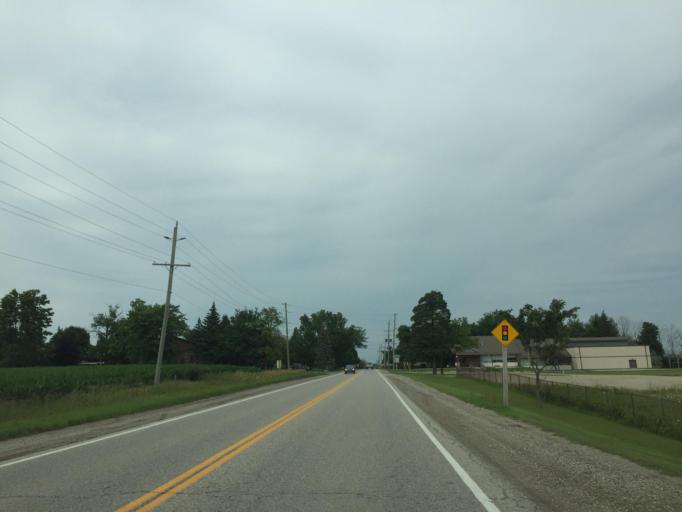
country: CA
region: Ontario
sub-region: Wellington County
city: Guelph
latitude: 43.5835
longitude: -80.3027
